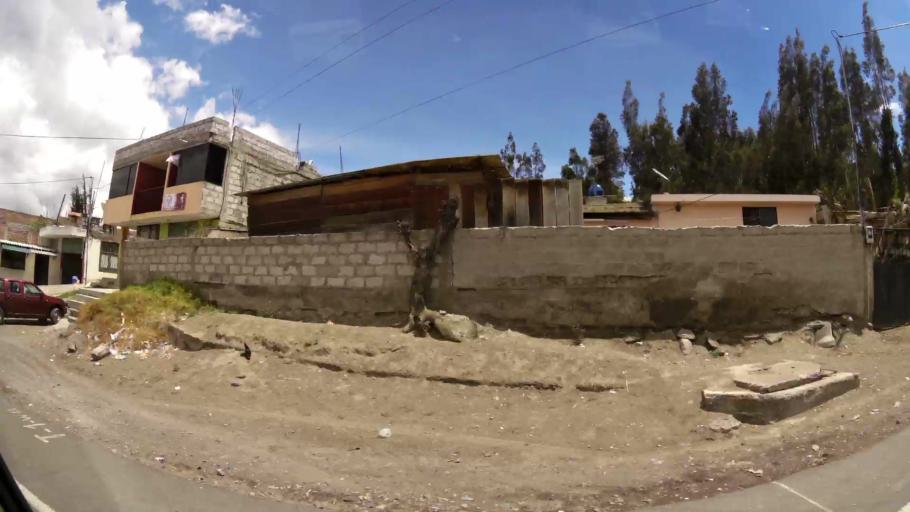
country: EC
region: Tungurahua
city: Ambato
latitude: -1.2768
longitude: -78.5859
